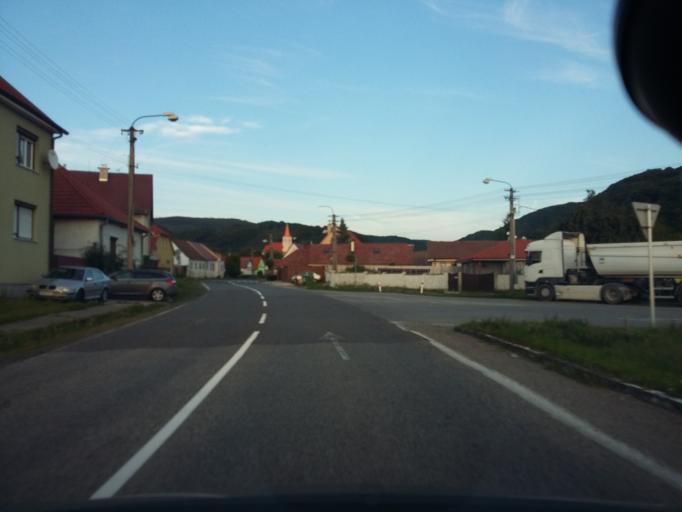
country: SK
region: Bratislavsky
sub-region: Okres Malacky
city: Malacky
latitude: 48.3689
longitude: 17.1397
